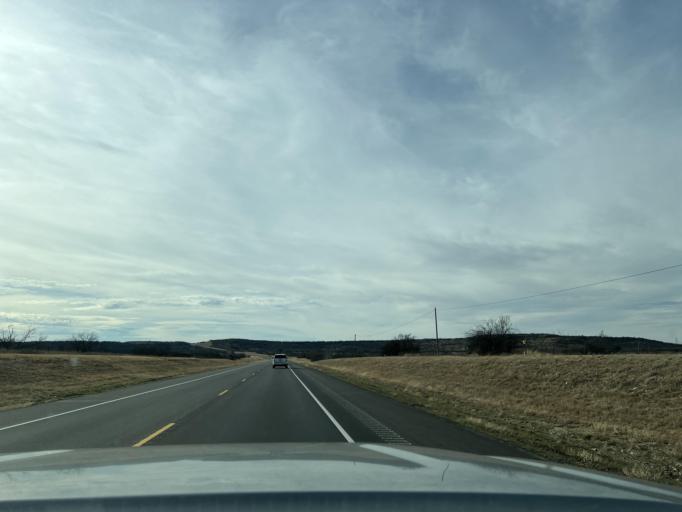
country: US
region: Texas
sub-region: Shackelford County
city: Albany
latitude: 32.7129
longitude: -99.3523
